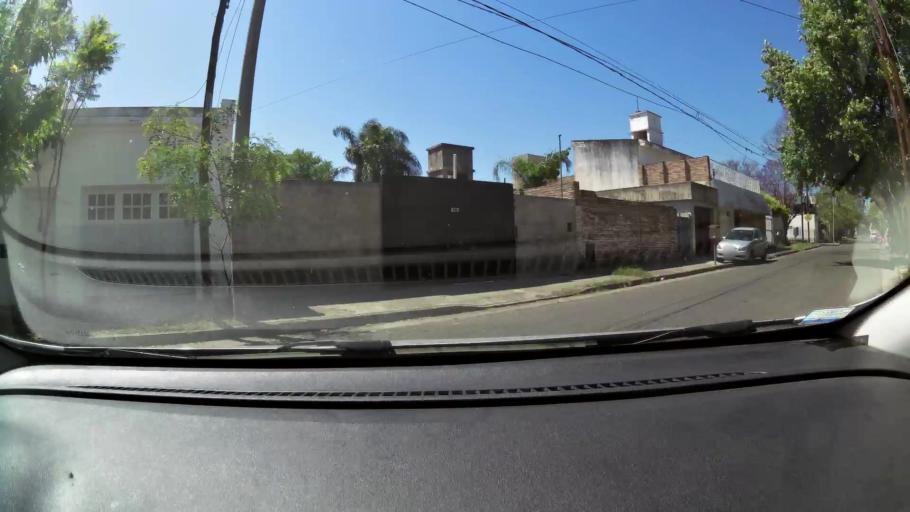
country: AR
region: Cordoba
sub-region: Departamento de Capital
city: Cordoba
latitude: -31.4194
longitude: -64.2122
